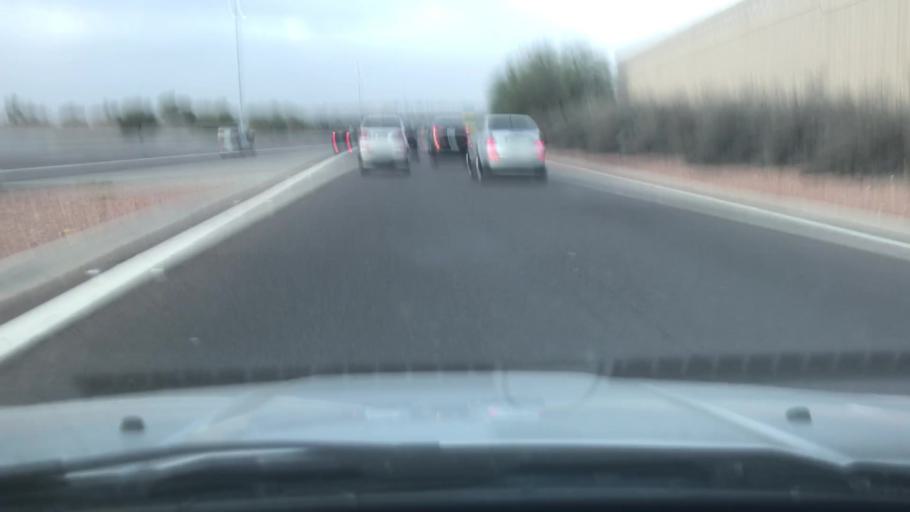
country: US
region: Arizona
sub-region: Maricopa County
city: Chandler
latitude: 33.3101
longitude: -111.8940
